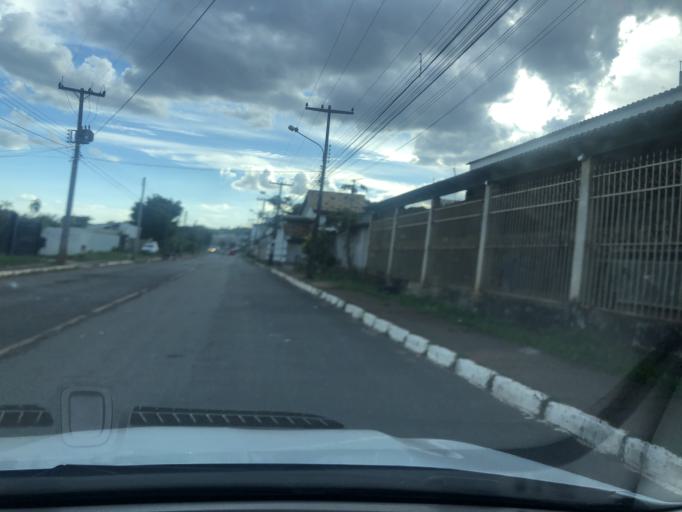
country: BR
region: Federal District
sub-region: Brasilia
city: Brasilia
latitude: -15.8741
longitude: -47.9701
